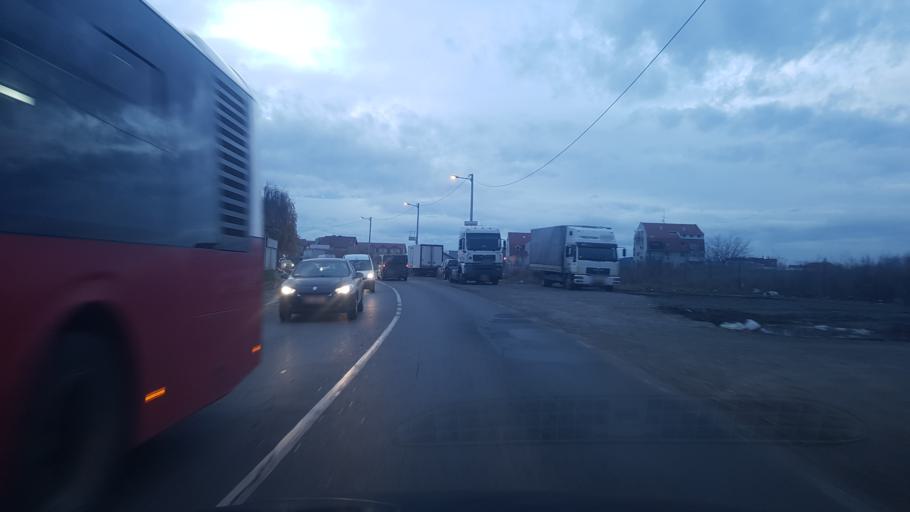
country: RS
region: Central Serbia
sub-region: Belgrade
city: Zemun
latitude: 44.8079
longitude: 20.3579
